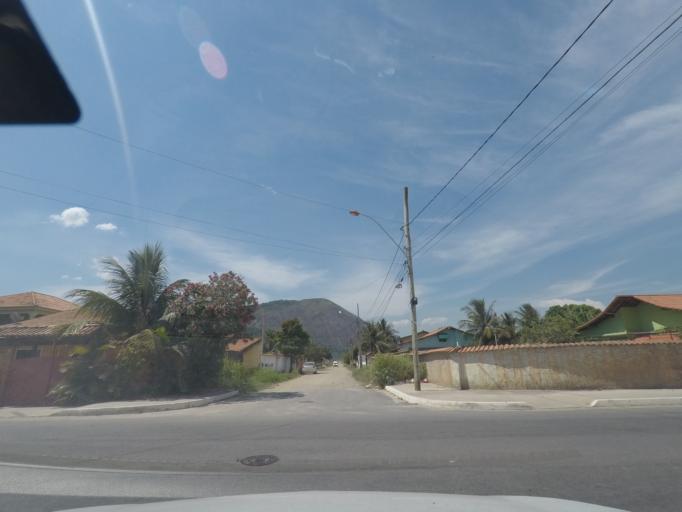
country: BR
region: Rio de Janeiro
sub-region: Marica
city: Marica
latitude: -22.9568
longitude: -42.9604
